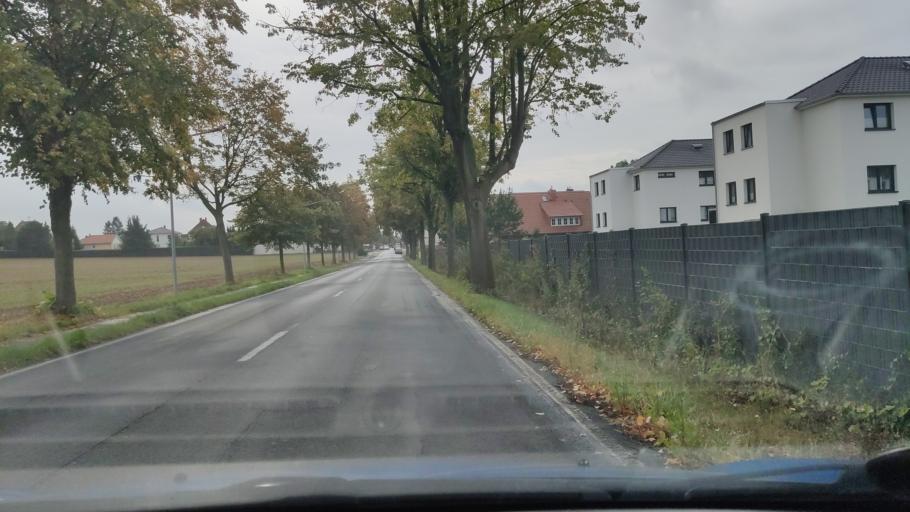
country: DE
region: Lower Saxony
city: Ronnenberg
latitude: 52.3741
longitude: 9.6512
